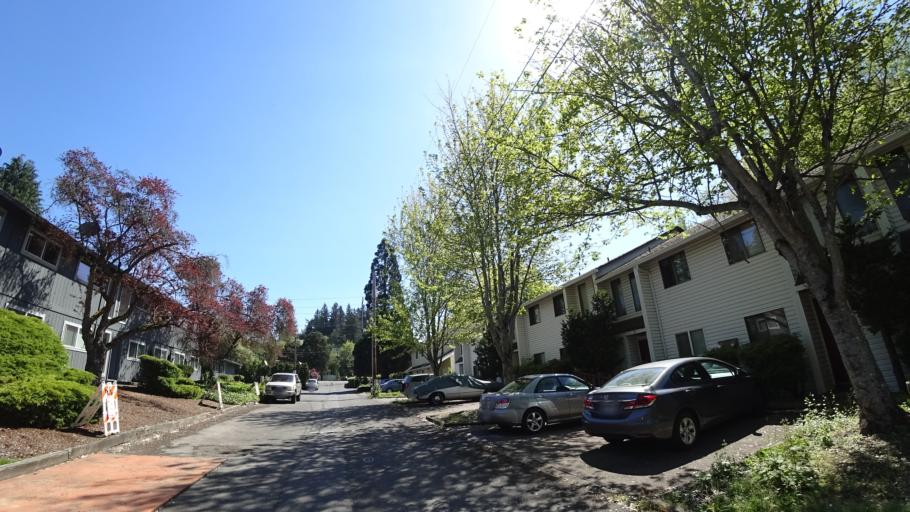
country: US
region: Oregon
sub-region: Washington County
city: Raleigh Hills
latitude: 45.4880
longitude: -122.7380
